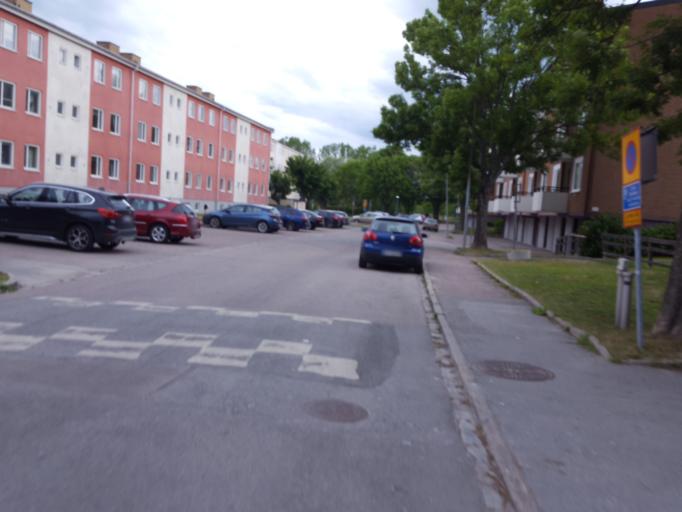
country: SE
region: Uppsala
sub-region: Uppsala Kommun
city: Uppsala
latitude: 59.8730
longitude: 17.6661
